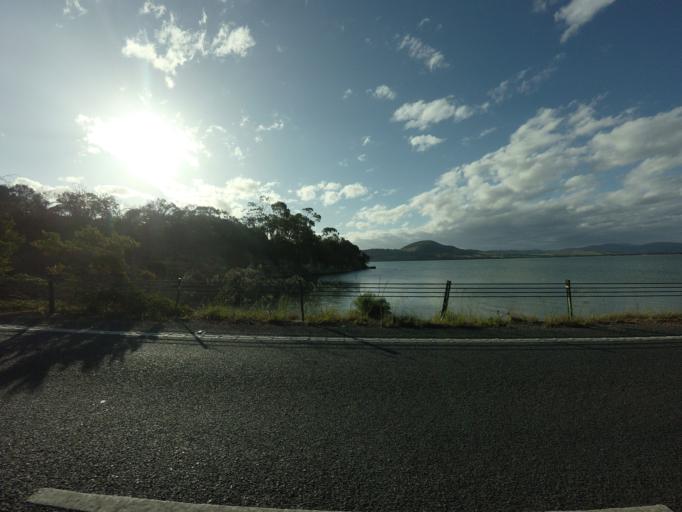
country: AU
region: Tasmania
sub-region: Clarence
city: Seven Mile Beach
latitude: -42.8130
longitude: 147.5148
